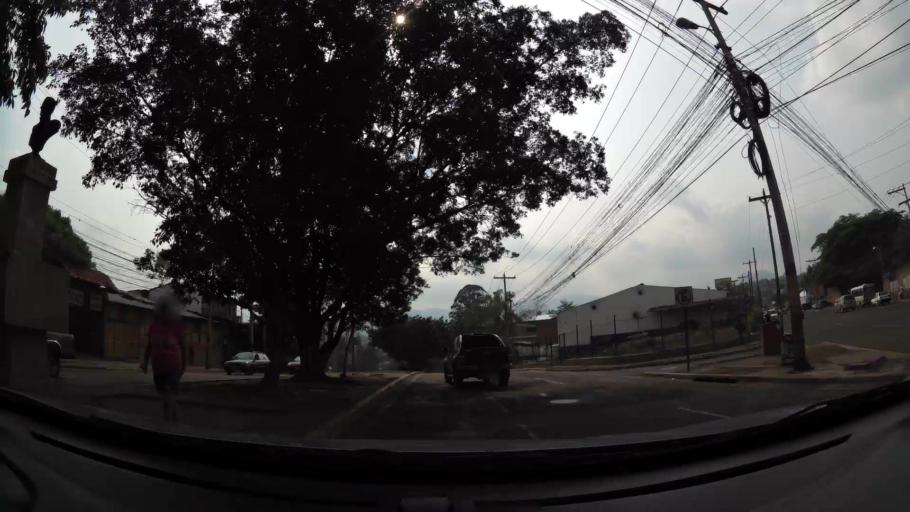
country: HN
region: Francisco Morazan
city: Tegucigalpa
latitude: 14.1031
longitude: -87.1772
